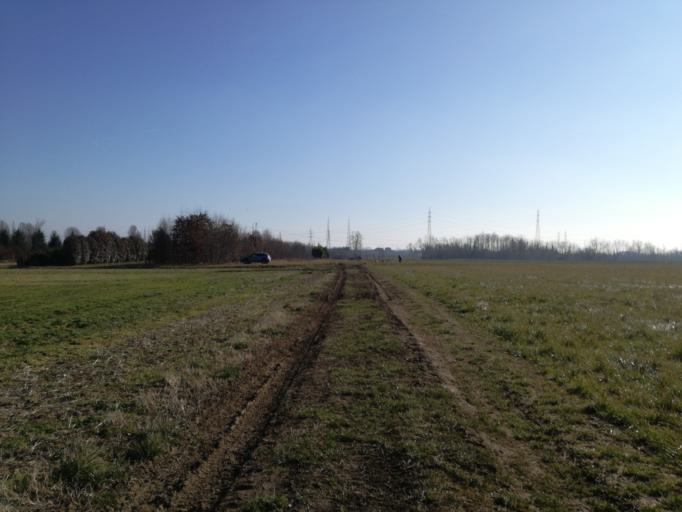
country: IT
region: Lombardy
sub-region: Provincia di Lecco
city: Verderio Inferiore
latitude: 45.6518
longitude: 9.4368
